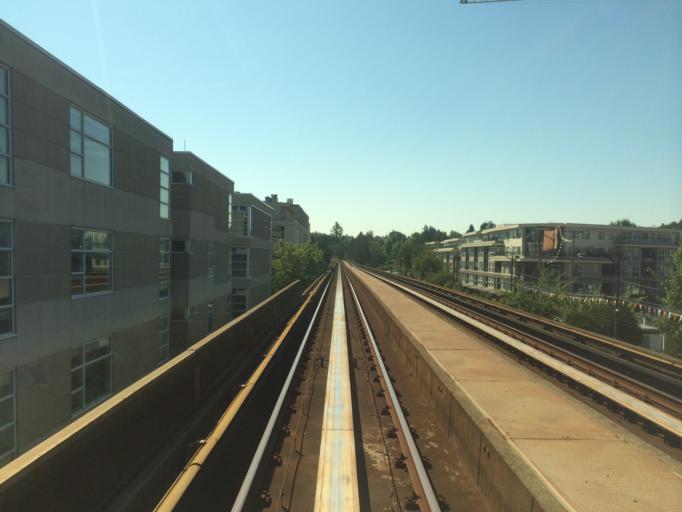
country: CA
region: British Columbia
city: Vancouver
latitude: 49.2542
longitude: -123.0677
